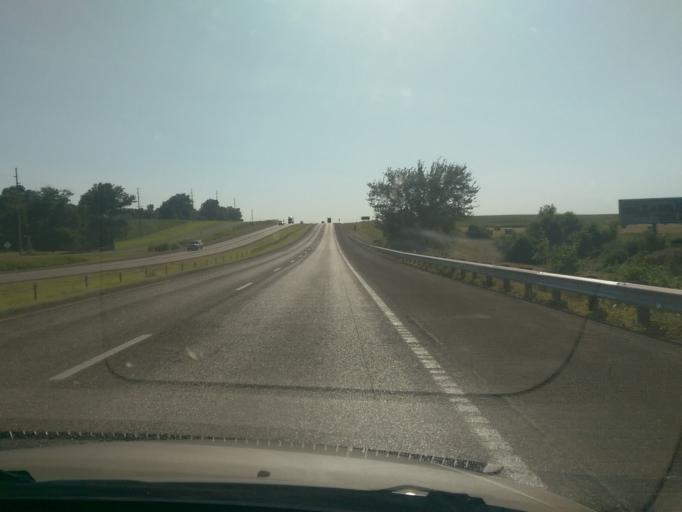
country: US
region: Missouri
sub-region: Lafayette County
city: Concordia
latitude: 38.9940
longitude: -93.5968
